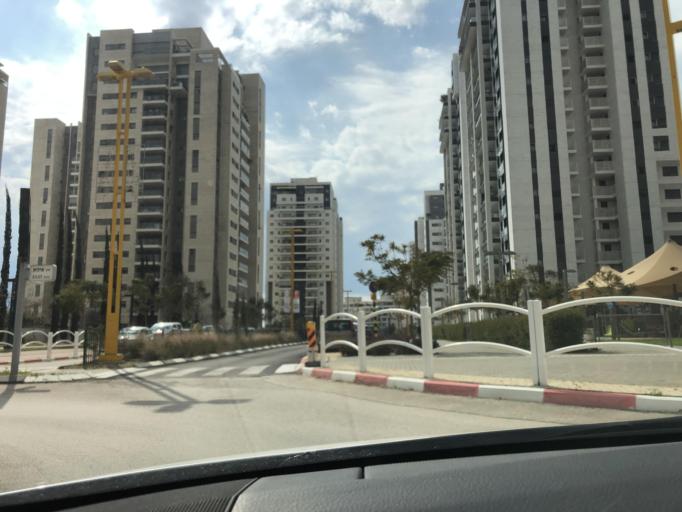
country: IL
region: Central District
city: Ganne Tiqwa
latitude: 32.0648
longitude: 34.8699
